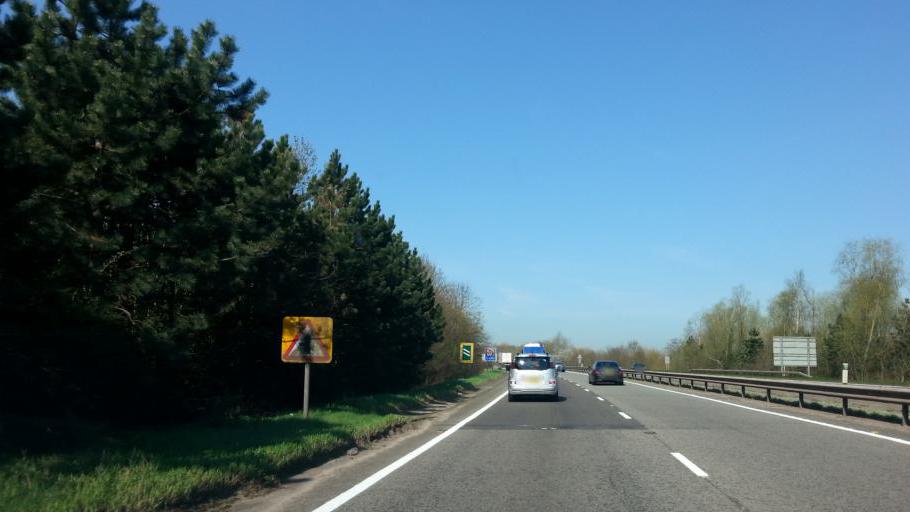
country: GB
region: England
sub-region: Derbyshire
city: Rodsley
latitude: 52.8840
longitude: -1.7260
